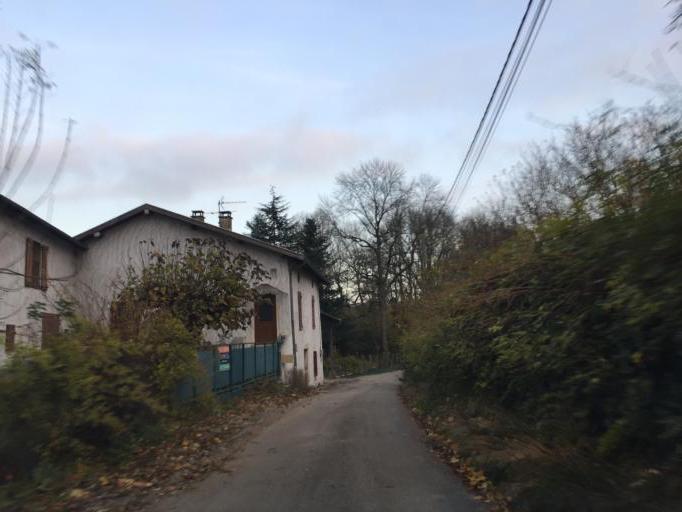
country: FR
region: Rhone-Alpes
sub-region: Departement de l'Ain
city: Chatillon-la-Palud
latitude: 45.9426
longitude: 5.2467
